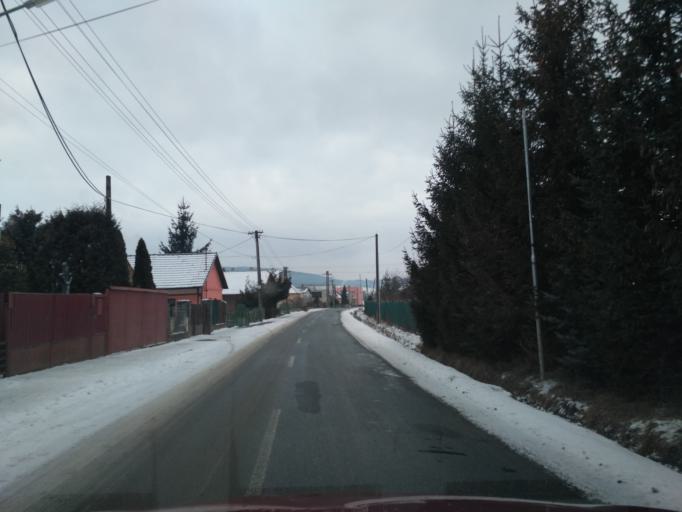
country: SK
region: Presovsky
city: Sabinov
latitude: 49.0141
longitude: 21.1207
